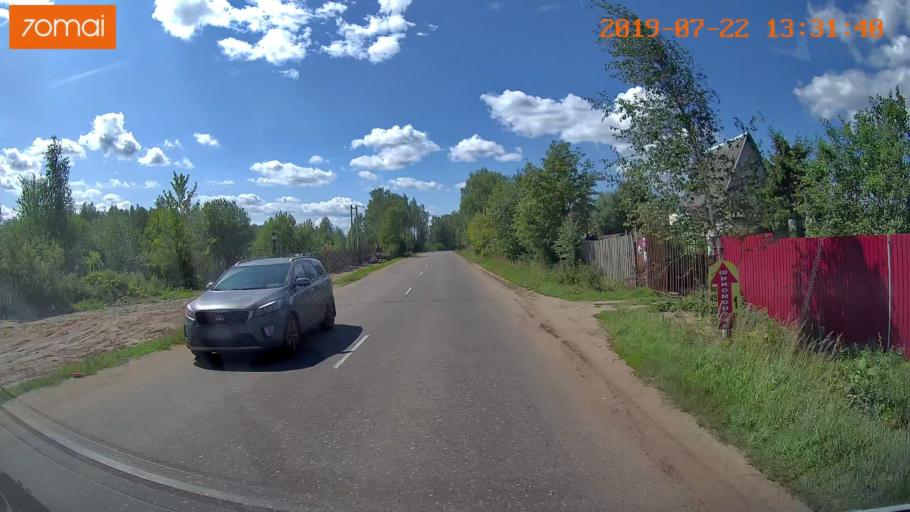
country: RU
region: Ivanovo
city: Novo-Talitsy
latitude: 57.0586
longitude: 40.9104
